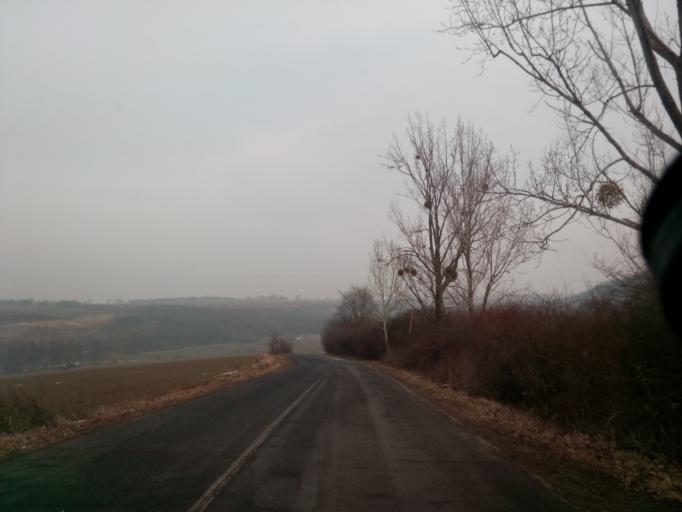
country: HU
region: Borsod-Abauj-Zemplen
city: Gonc
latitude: 48.4916
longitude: 21.2993
